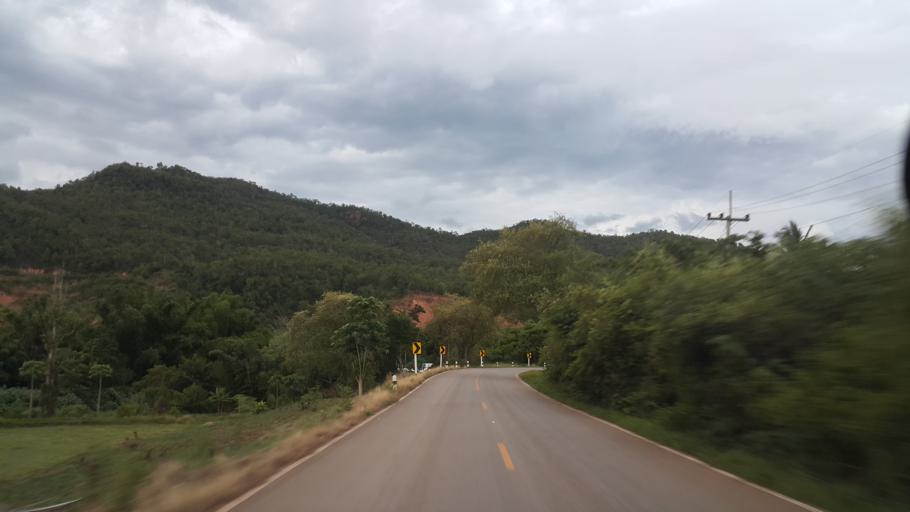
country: TH
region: Loei
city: Na Haeo
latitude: 17.5278
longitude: 101.1853
